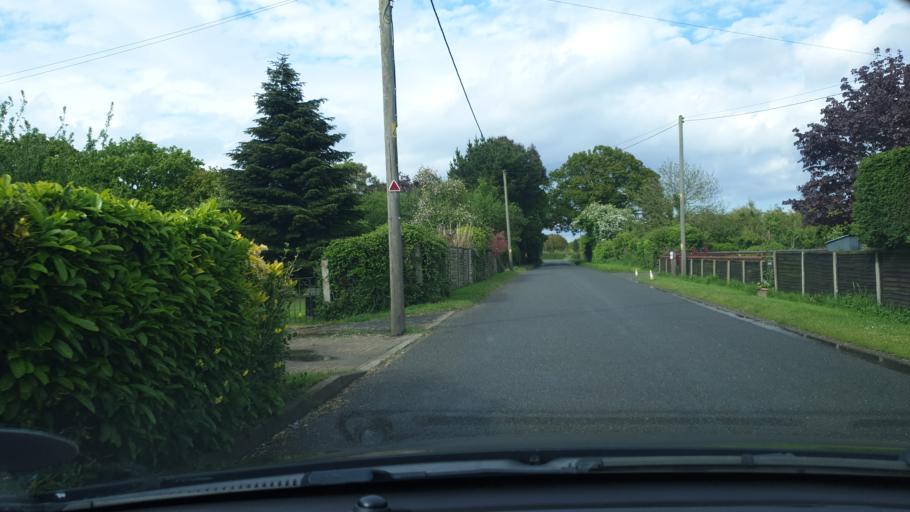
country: GB
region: England
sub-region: Essex
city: Little Clacton
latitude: 51.8319
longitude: 1.1174
